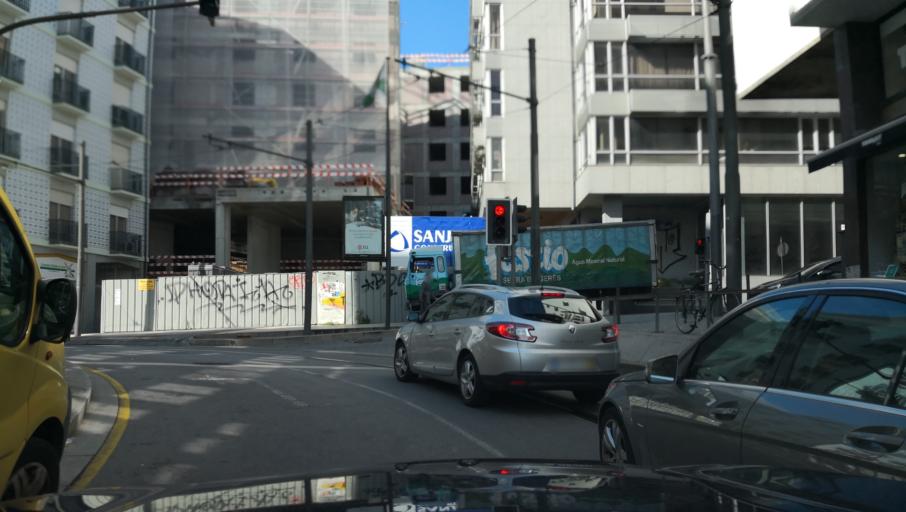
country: PT
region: Porto
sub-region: Porto
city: Porto
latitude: 41.1484
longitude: -8.6141
